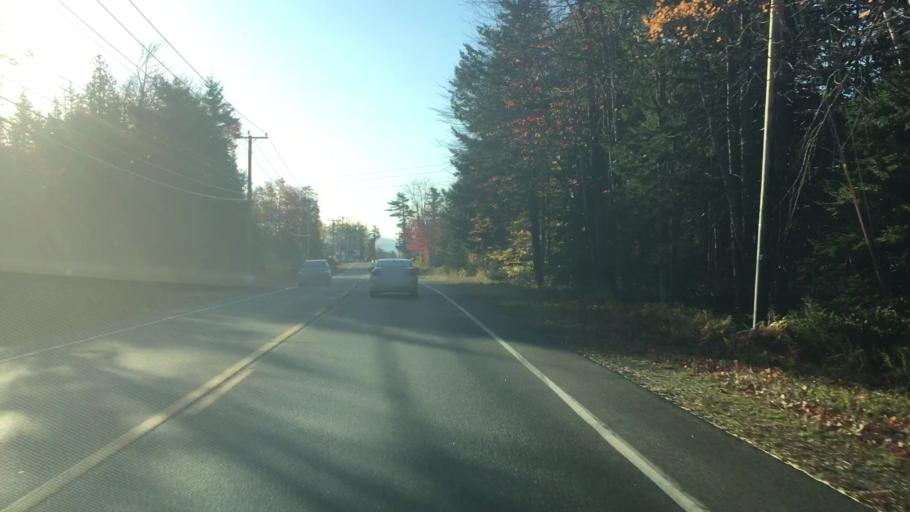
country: US
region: Maine
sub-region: Hancock County
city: Ellsworth
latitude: 44.5113
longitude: -68.3924
